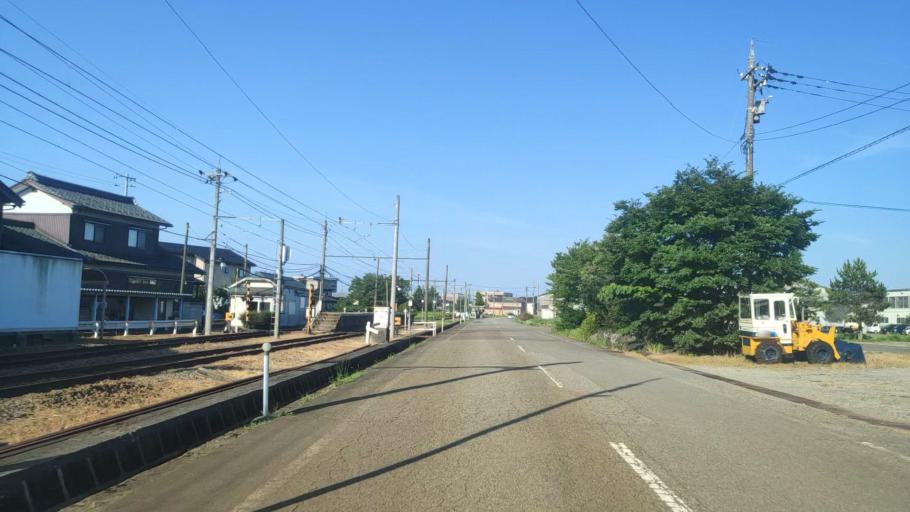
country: JP
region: Fukui
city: Fukui-shi
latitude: 36.0829
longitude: 136.2619
